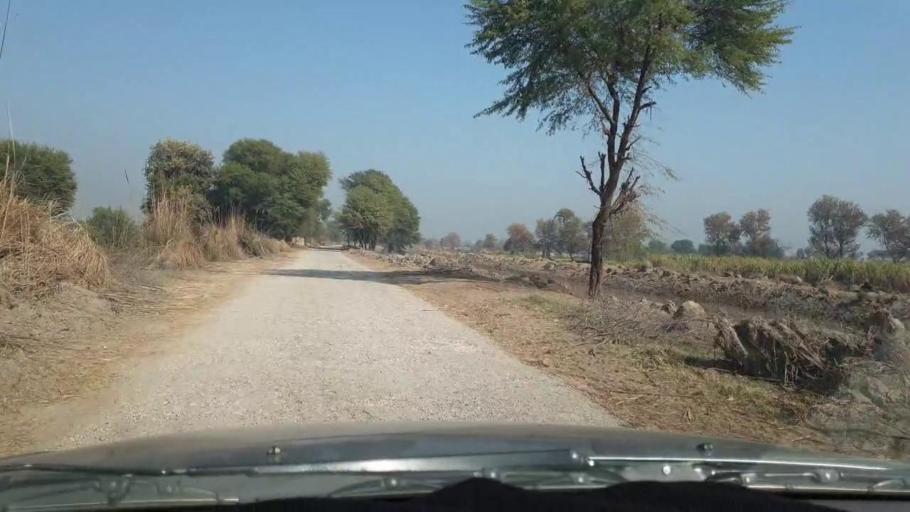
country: PK
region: Sindh
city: Khanpur
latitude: 27.7727
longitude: 69.5353
